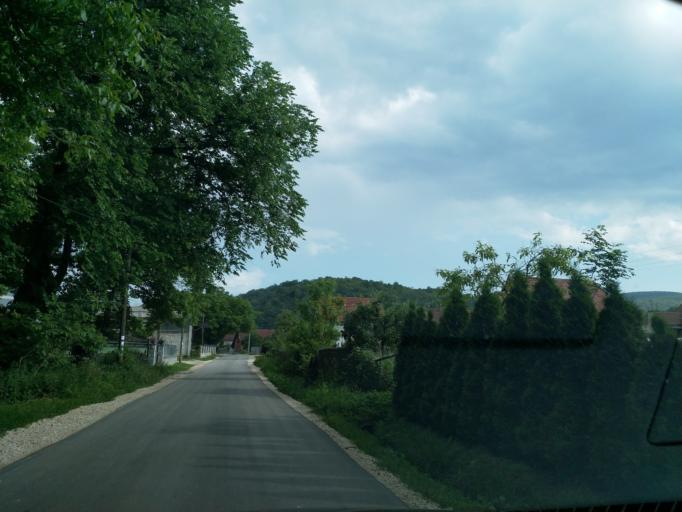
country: RS
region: Central Serbia
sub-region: Borski Okrug
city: Bor
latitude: 44.0189
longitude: 21.9809
